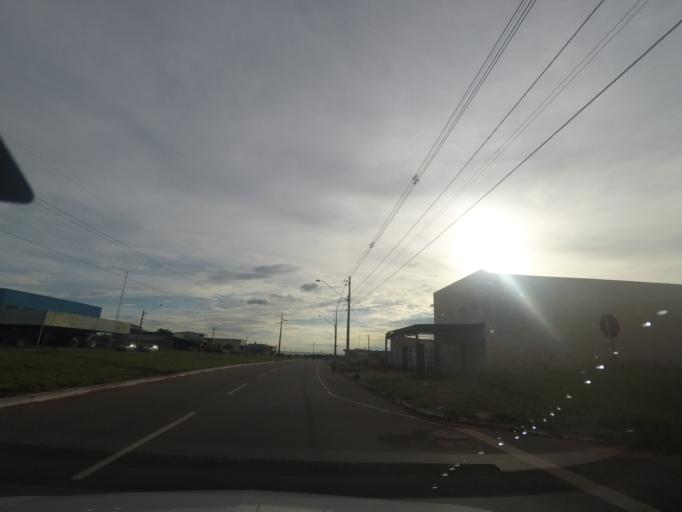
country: BR
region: Goias
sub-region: Trindade
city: Trindade
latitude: -16.7216
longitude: -49.3993
